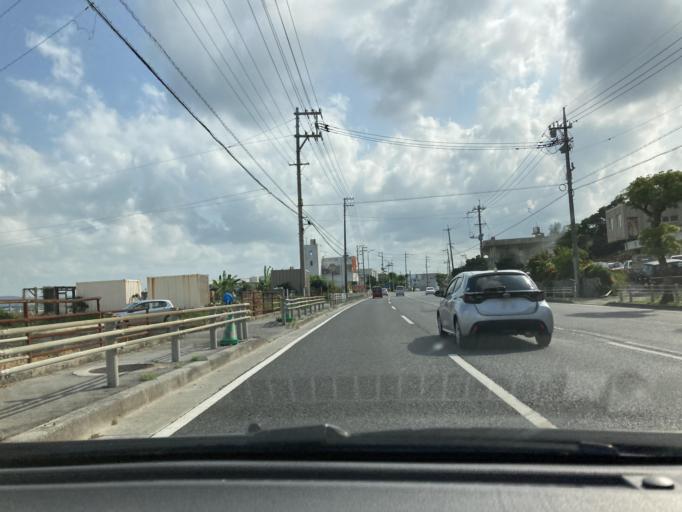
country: JP
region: Okinawa
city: Ginowan
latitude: 26.2465
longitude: 127.7818
